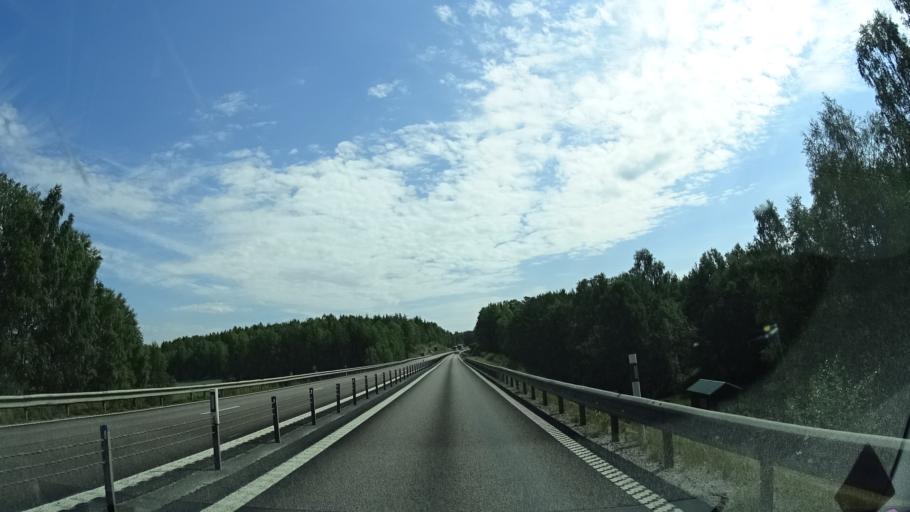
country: SE
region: Vaermland
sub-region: Karlstads Kommun
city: Skattkarr
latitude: 59.4208
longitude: 13.6945
